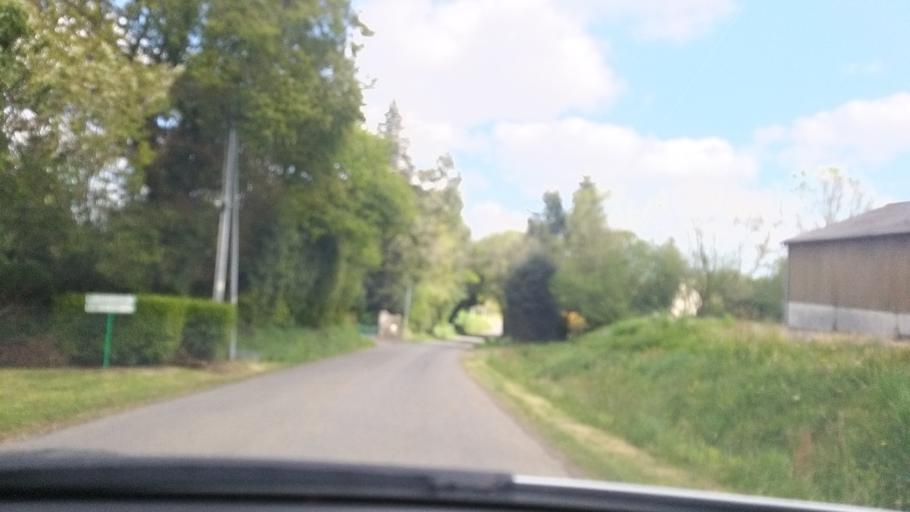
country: FR
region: Brittany
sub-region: Departement du Finistere
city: Huelgoat
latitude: 48.3539
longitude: -3.7118
